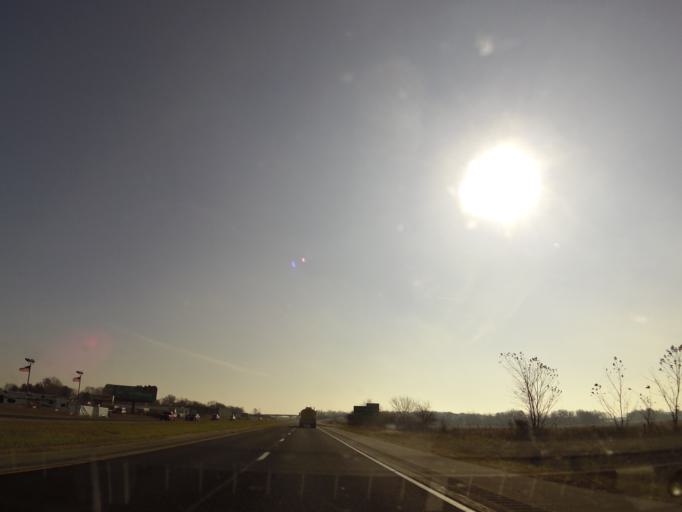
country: US
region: Indiana
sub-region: Hancock County
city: New Palestine
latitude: 39.6665
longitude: -85.9493
